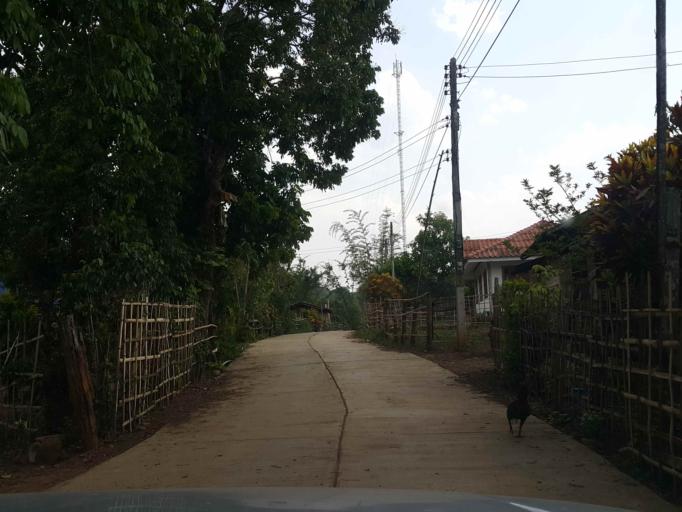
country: TH
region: Chiang Mai
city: Wiang Haeng
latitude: 19.3774
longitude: 98.7208
